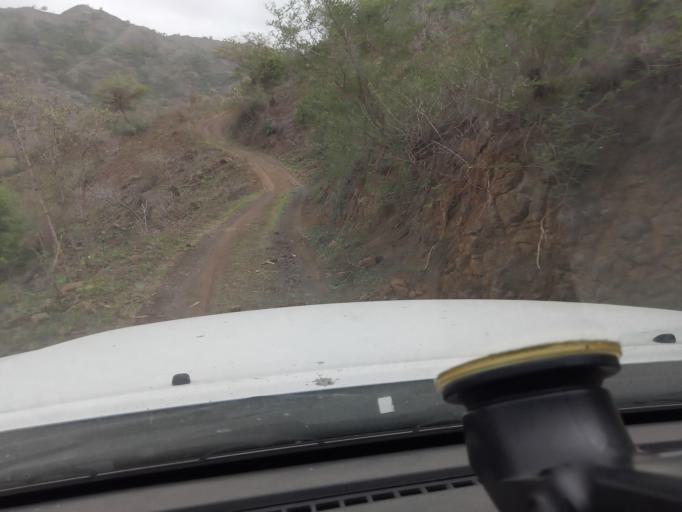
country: CV
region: Sao Salvador do Mundo
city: Picos
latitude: 15.1417
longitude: -23.6346
